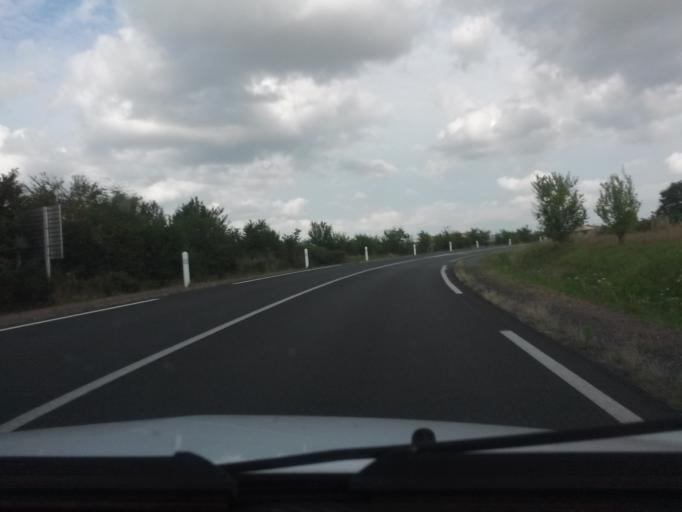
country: FR
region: Pays de la Loire
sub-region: Departement de la Vendee
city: La Bruffiere
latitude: 47.0080
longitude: -1.1882
